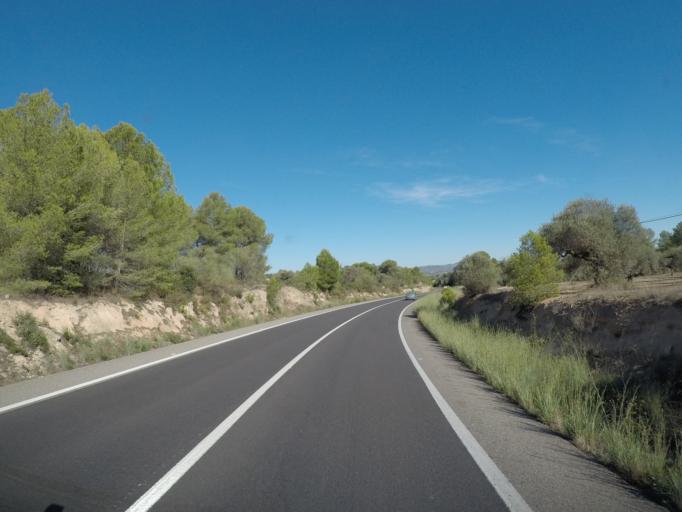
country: ES
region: Catalonia
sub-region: Provincia de Tarragona
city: Rasquera
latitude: 41.0184
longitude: 0.6084
